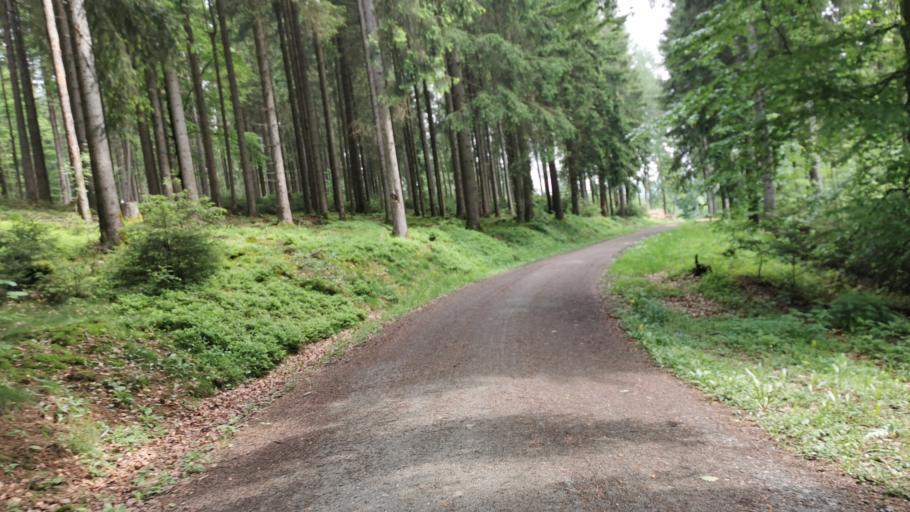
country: DE
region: Bavaria
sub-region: Upper Franconia
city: Ludwigsstadt
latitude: 50.4467
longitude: 11.3666
